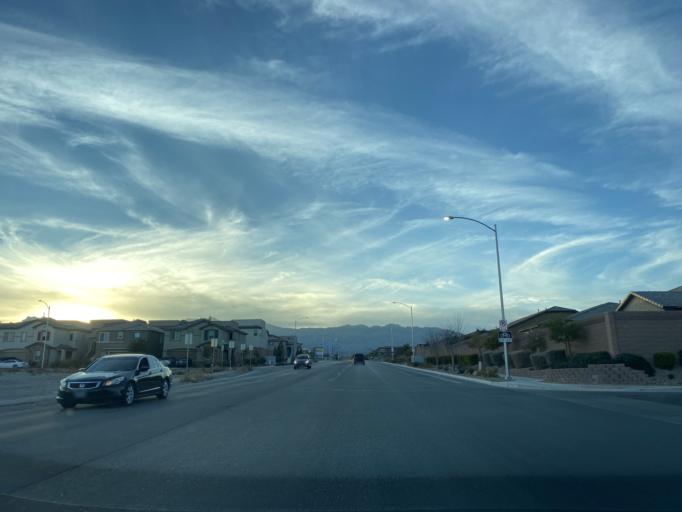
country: US
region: Nevada
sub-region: Clark County
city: Summerlin South
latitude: 36.2847
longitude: -115.3096
